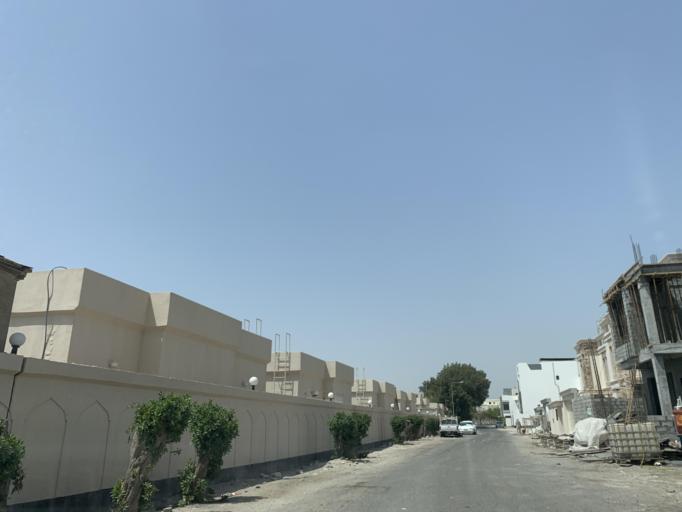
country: BH
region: Manama
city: Manama
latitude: 26.1978
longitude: 50.5640
